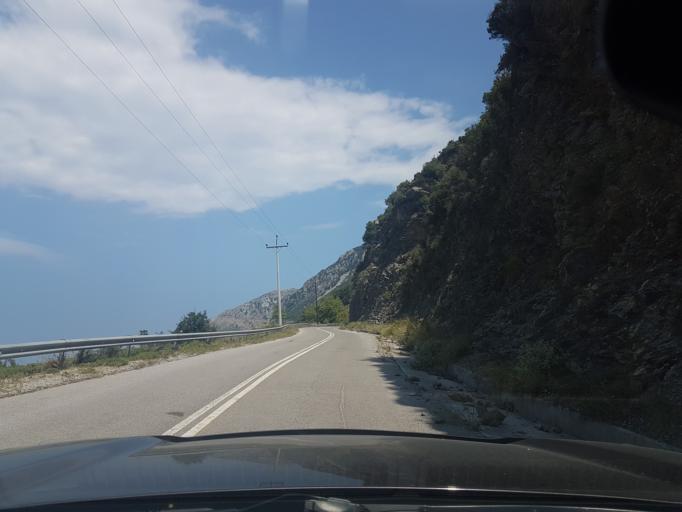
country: GR
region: Central Greece
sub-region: Nomos Evvoias
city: Kymi
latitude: 38.6350
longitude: 23.9545
